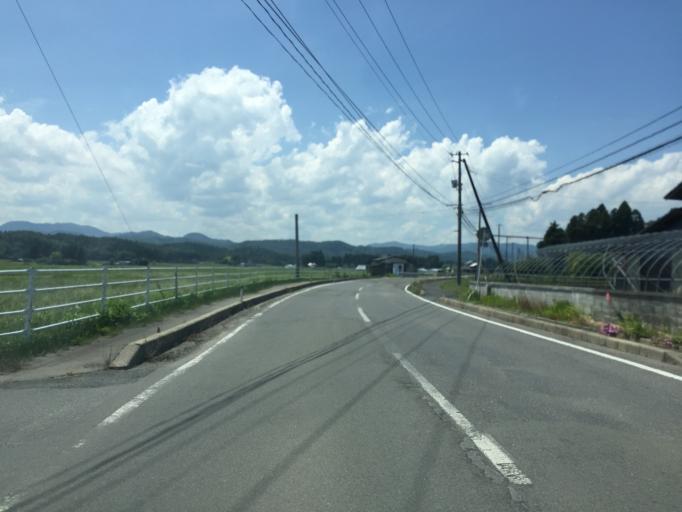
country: JP
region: Fukushima
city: Namie
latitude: 37.7127
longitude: 140.9479
